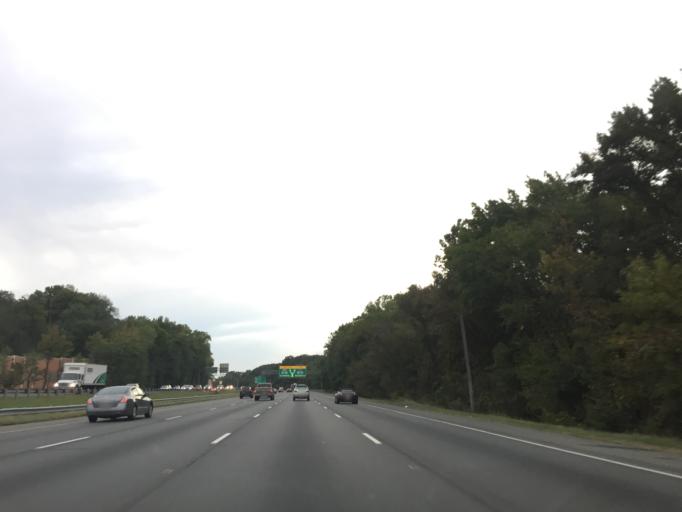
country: US
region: Maryland
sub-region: Prince George's County
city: Temple Hills
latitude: 38.8181
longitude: -76.9399
